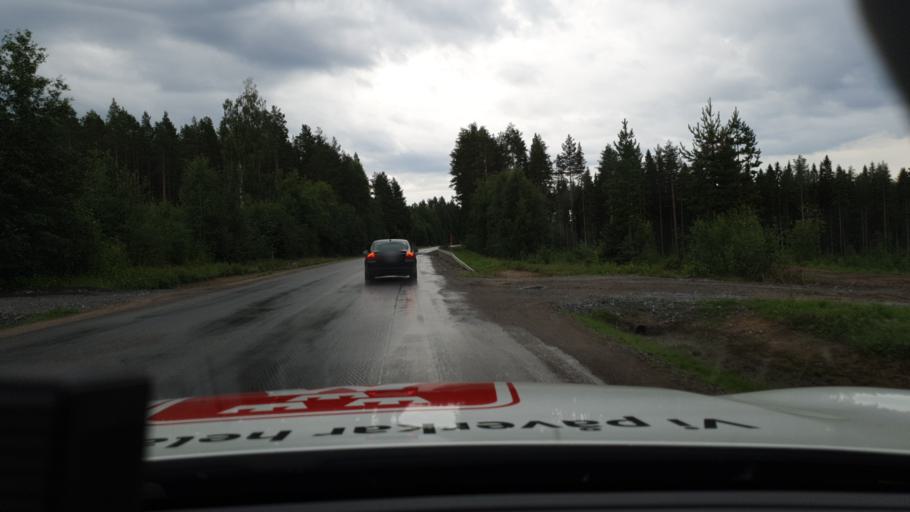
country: SE
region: Norrbotten
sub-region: Bodens Kommun
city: Boden
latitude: 65.8774
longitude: 21.4071
